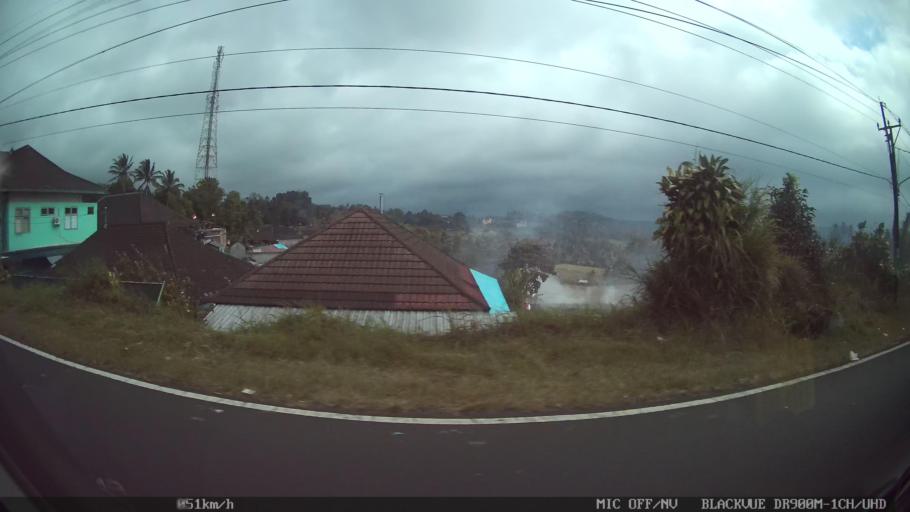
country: ID
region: Bali
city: Bantiran
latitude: -8.3122
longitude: 115.0026
